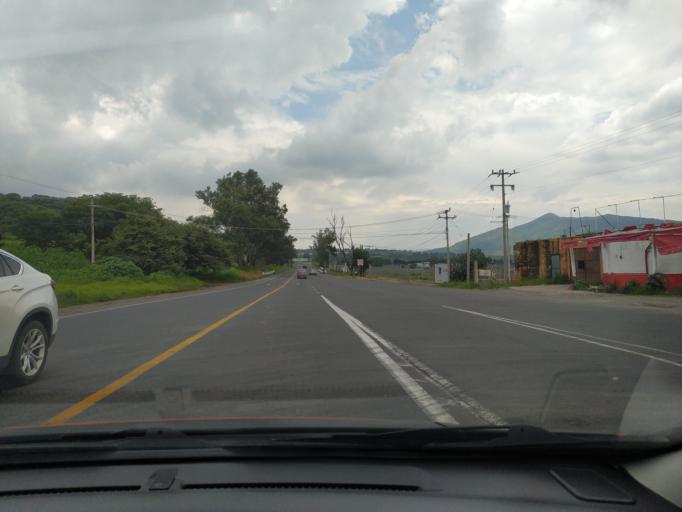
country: MX
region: Jalisco
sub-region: Acatlan de Juarez
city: Villa de los Ninos
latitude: 20.4223
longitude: -103.5520
